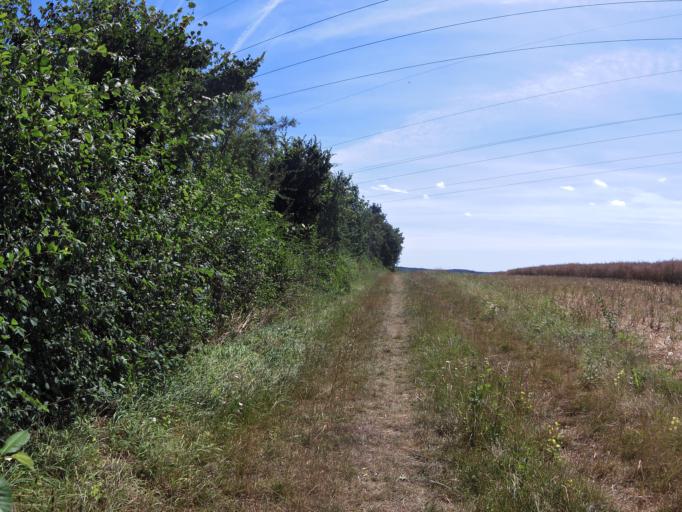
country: DE
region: Bavaria
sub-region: Regierungsbezirk Unterfranken
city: Hettstadt
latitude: 49.8140
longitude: 9.8314
